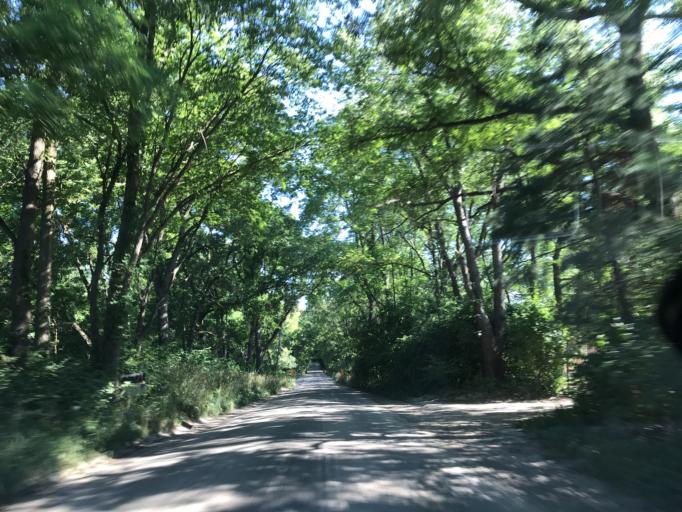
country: US
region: Michigan
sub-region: Washtenaw County
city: Ypsilanti
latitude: 42.2928
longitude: -83.6533
